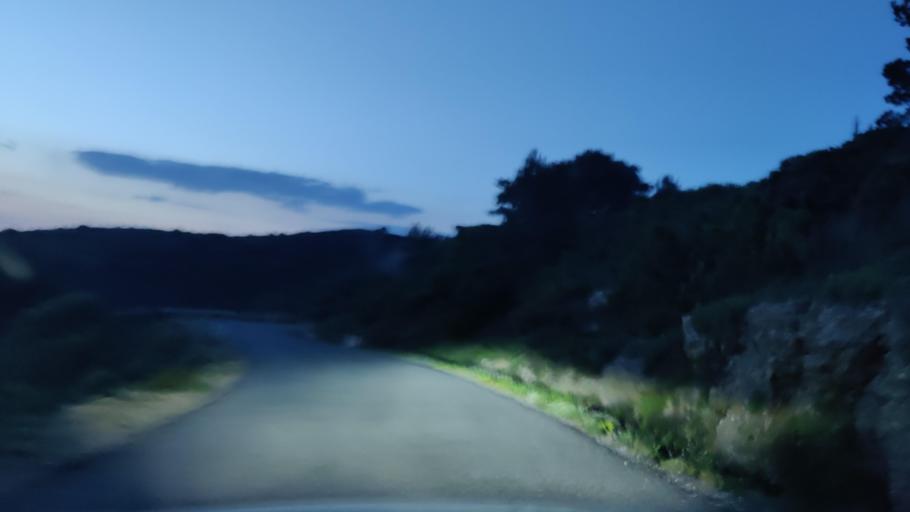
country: FR
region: Languedoc-Roussillon
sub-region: Departement des Pyrenees-Orientales
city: Estagel
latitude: 42.8797
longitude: 2.7534
